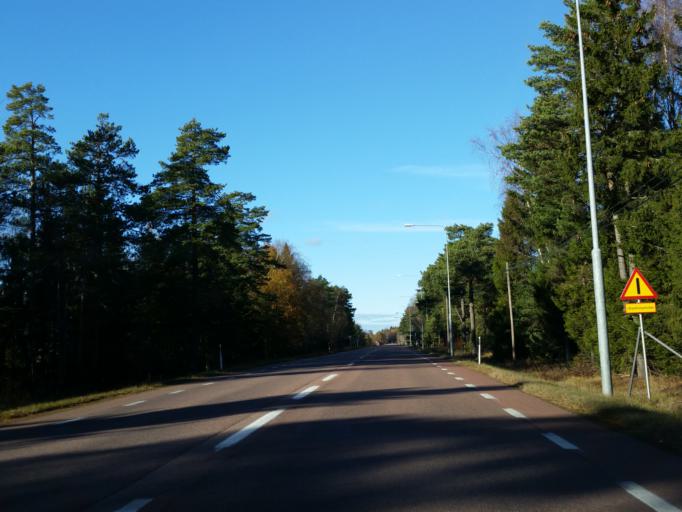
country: AX
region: Alands landsbygd
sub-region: Finstroem
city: Finstroem
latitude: 60.2360
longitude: 19.9792
